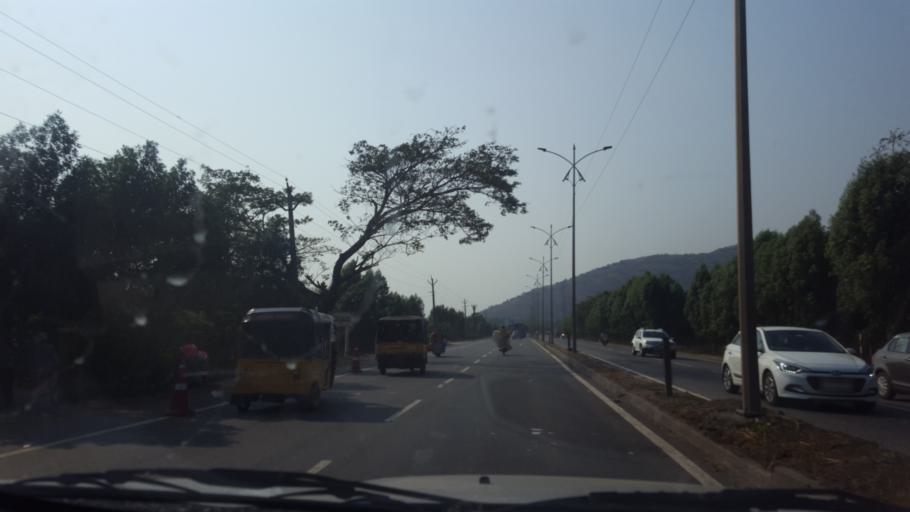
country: IN
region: Andhra Pradesh
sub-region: Vishakhapatnam
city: Anakapalle
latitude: 17.6864
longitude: 83.0806
